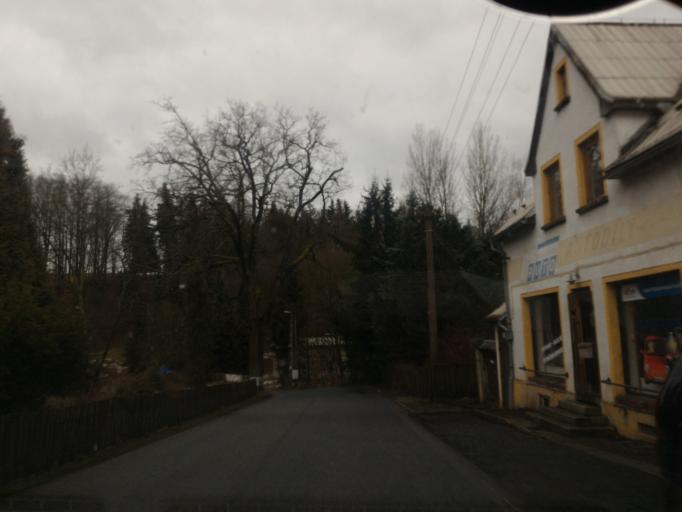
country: CZ
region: Ustecky
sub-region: Okres Decin
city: Krasna Lipa
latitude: 50.9217
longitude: 14.4897
